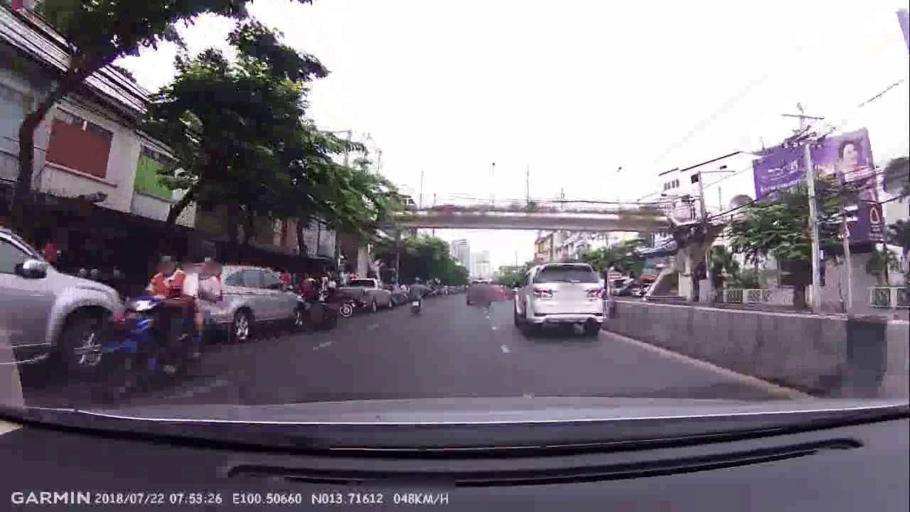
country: TH
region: Bangkok
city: Khlong San
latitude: 13.7160
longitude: 100.5065
